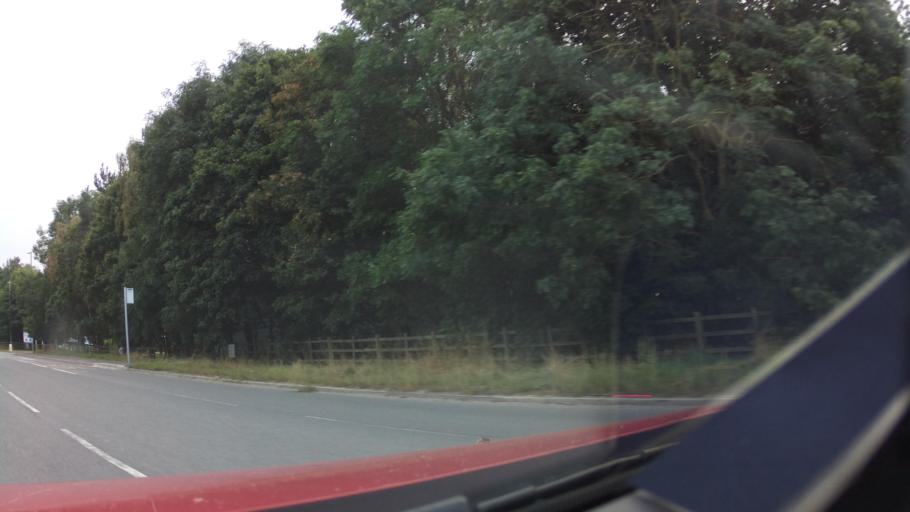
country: GB
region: England
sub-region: Nottinghamshire
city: South Collingham
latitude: 53.1512
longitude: -0.6703
